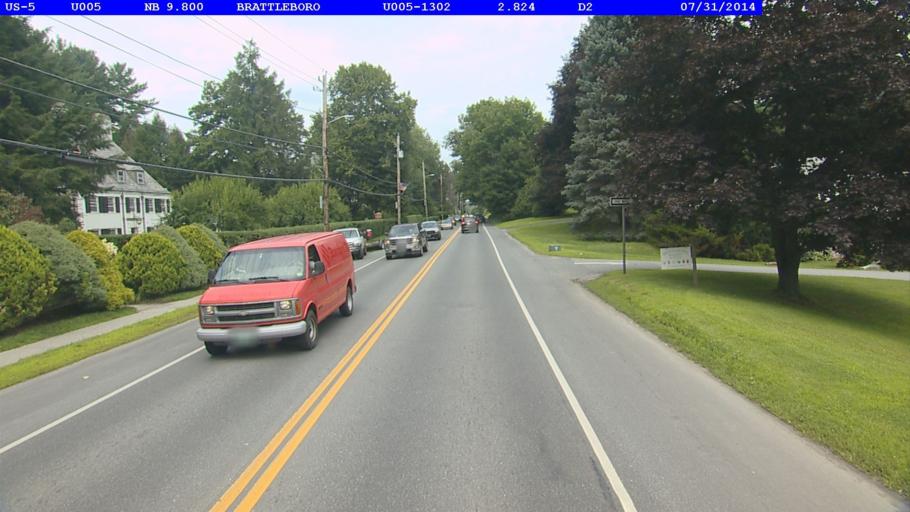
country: US
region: Vermont
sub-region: Windham County
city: Brattleboro
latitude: 42.8603
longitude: -72.5581
